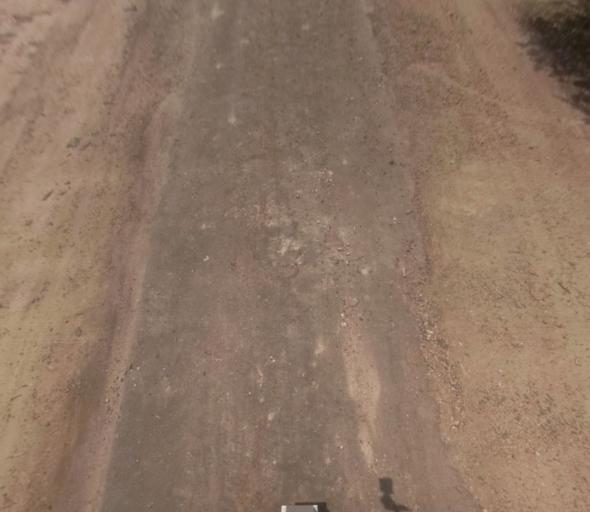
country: US
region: California
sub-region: Madera County
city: Parkwood
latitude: 36.9217
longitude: -120.0789
